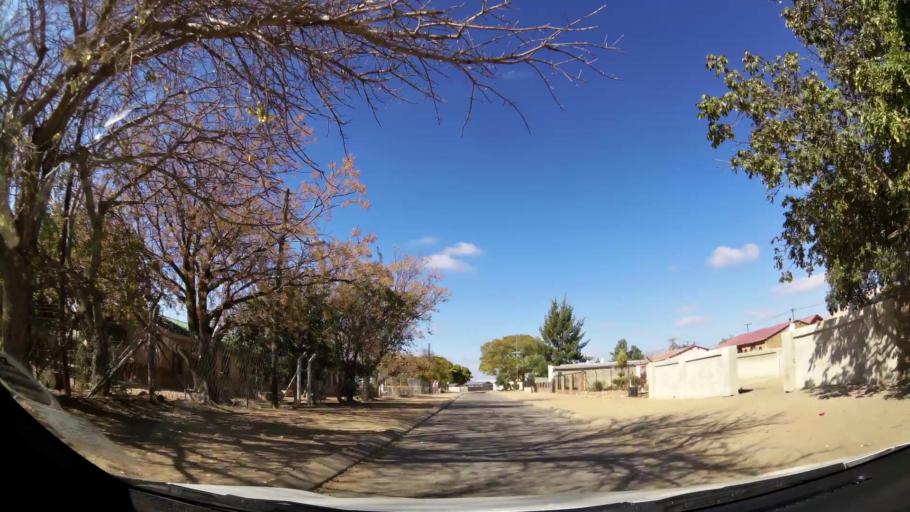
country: ZA
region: Limpopo
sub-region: Capricorn District Municipality
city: Polokwane
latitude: -23.8634
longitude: 29.3886
